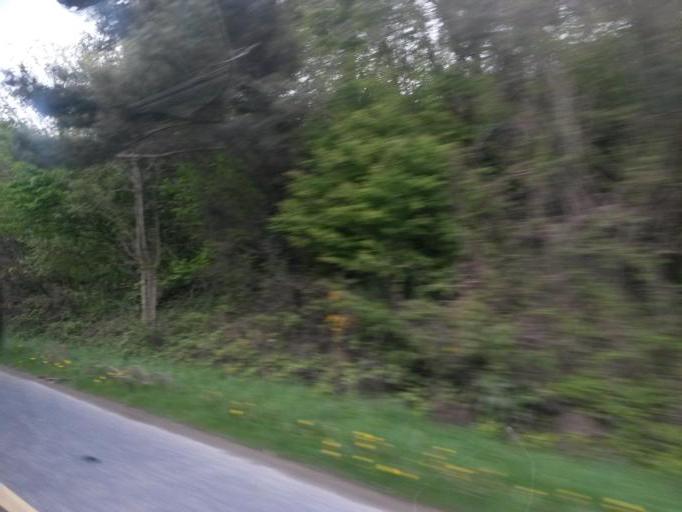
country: IE
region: Leinster
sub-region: Loch Garman
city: Enniscorthy
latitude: 52.4709
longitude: -6.5614
